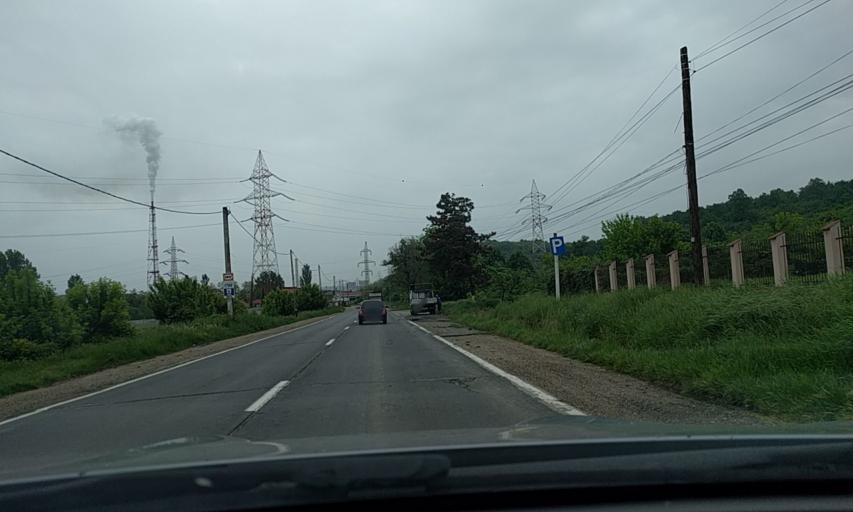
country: RO
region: Dambovita
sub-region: Comuna Aninoasa
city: Sateni
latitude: 44.9825
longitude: 25.4201
